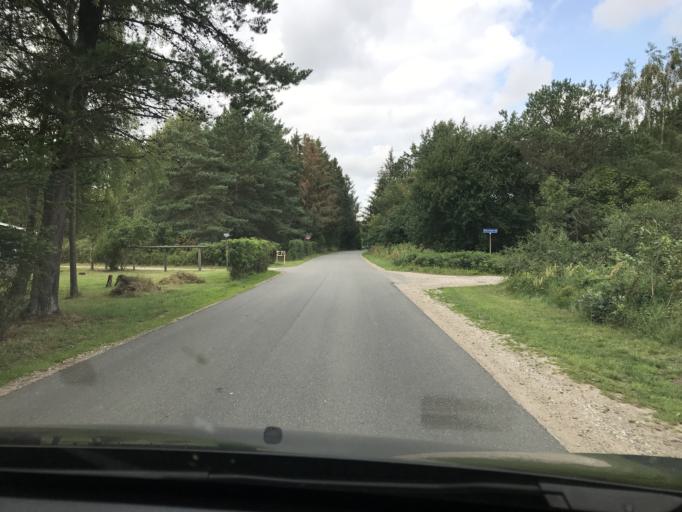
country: DK
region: Central Jutland
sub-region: Syddjurs Kommune
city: Ryomgard
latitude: 56.3593
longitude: 10.4468
